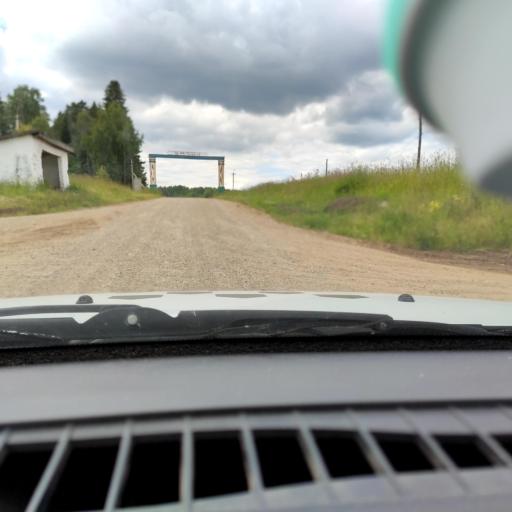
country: RU
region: Perm
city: Suksun
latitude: 57.2136
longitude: 57.6961
